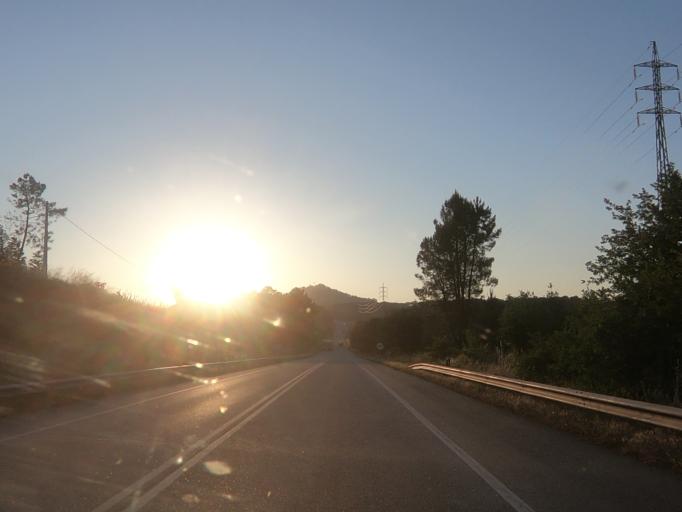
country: PT
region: Viseu
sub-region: Viseu
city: Abraveses
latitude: 40.6853
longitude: -7.8961
